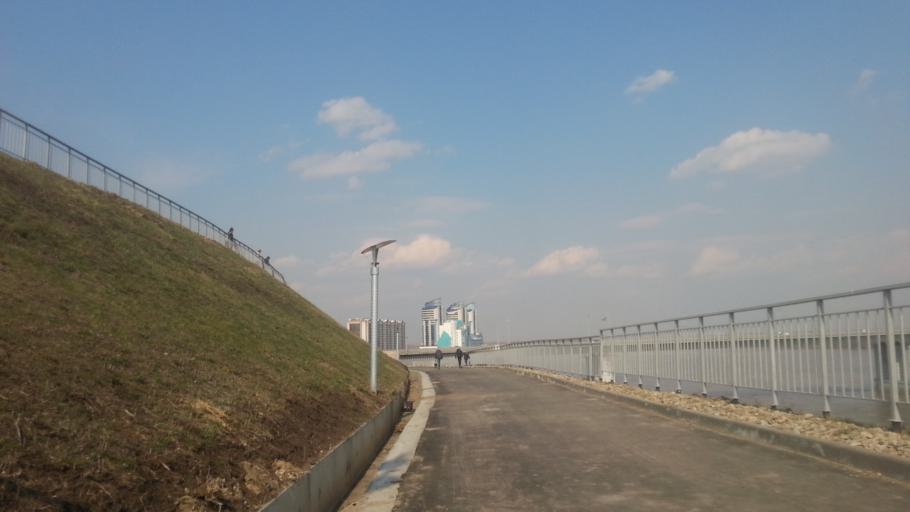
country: RU
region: Altai Krai
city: Zaton
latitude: 53.3225
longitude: 83.7970
